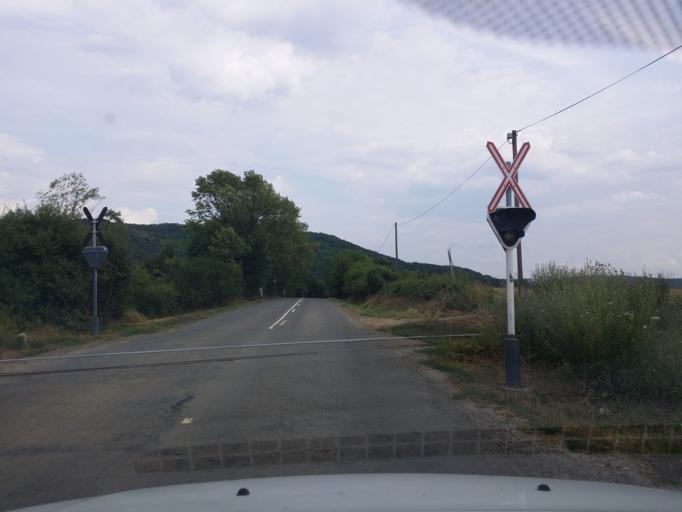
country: HU
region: Nograd
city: Romhany
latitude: 47.9579
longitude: 19.3528
